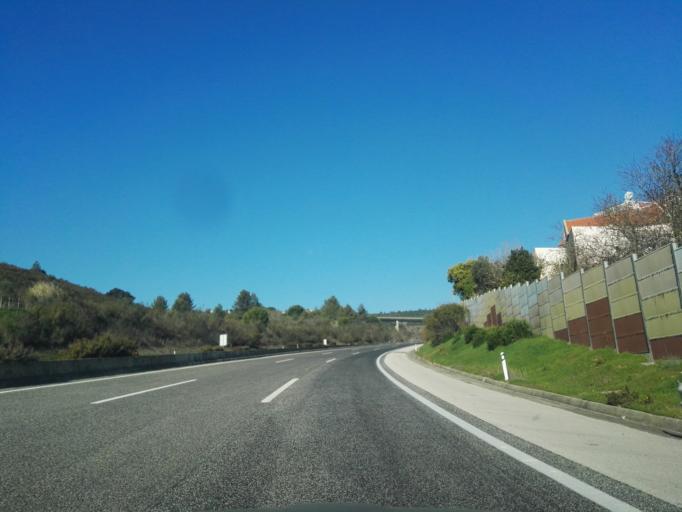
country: PT
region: Lisbon
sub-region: Vila Franca de Xira
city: Vialonga
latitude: 38.8990
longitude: -9.0553
